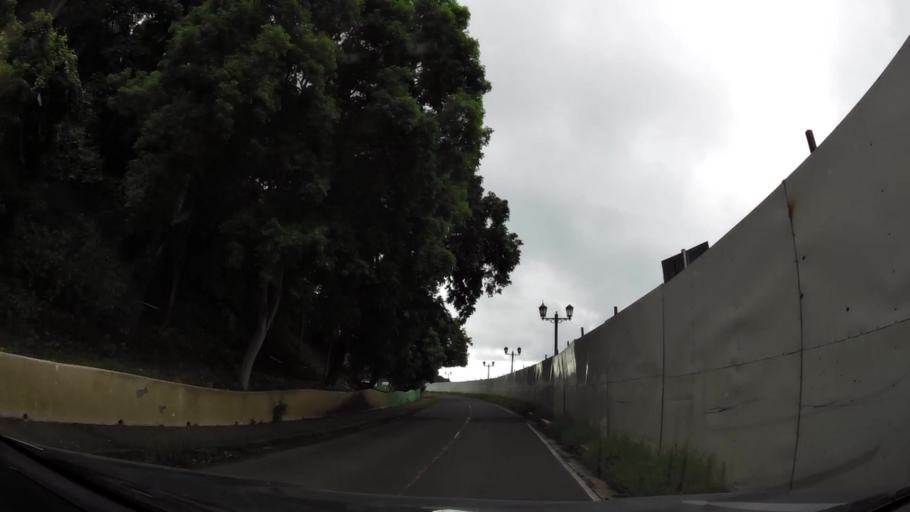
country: PA
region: Panama
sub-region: Distrito de Panama
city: Ancon
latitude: 8.9137
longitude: -79.5255
